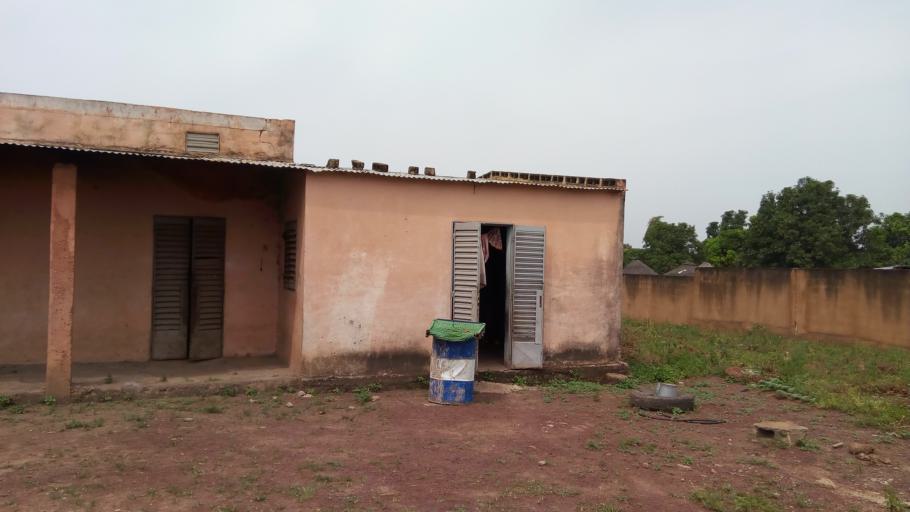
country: ML
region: Koulikoro
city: Kangaba
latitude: 11.4971
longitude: -8.5500
